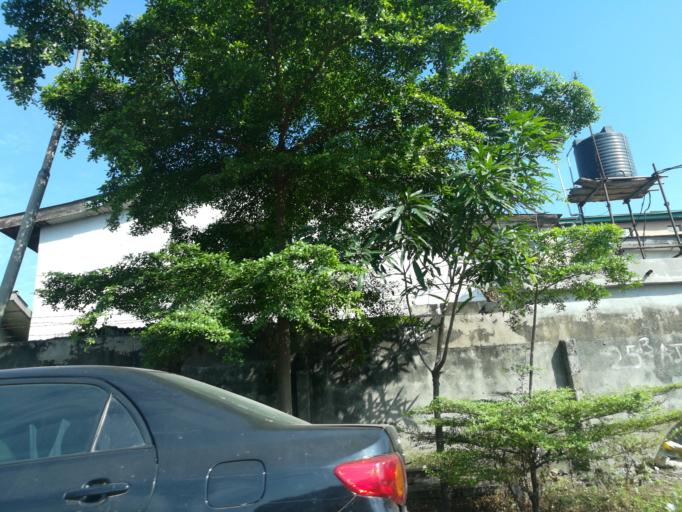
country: NG
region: Lagos
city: Ikeja
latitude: 6.6031
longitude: 3.3402
